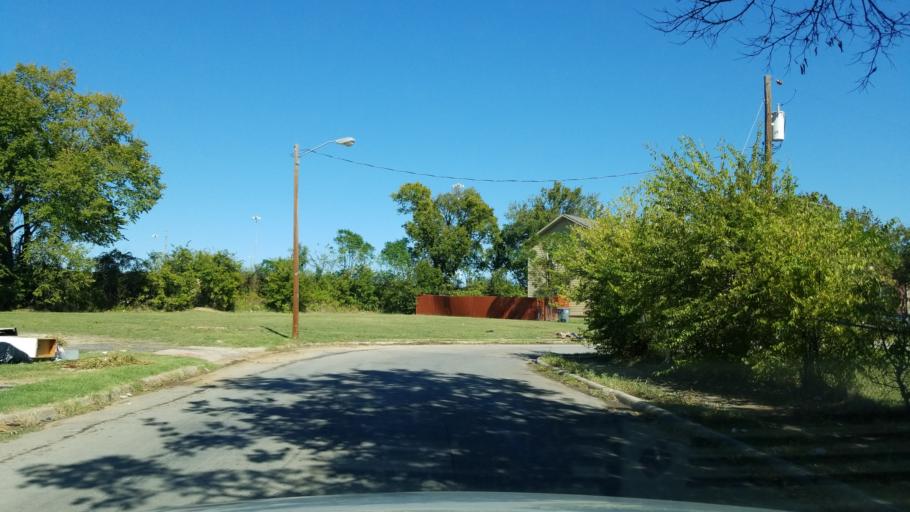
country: US
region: Texas
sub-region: Dallas County
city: Dallas
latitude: 32.7787
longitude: -96.7445
